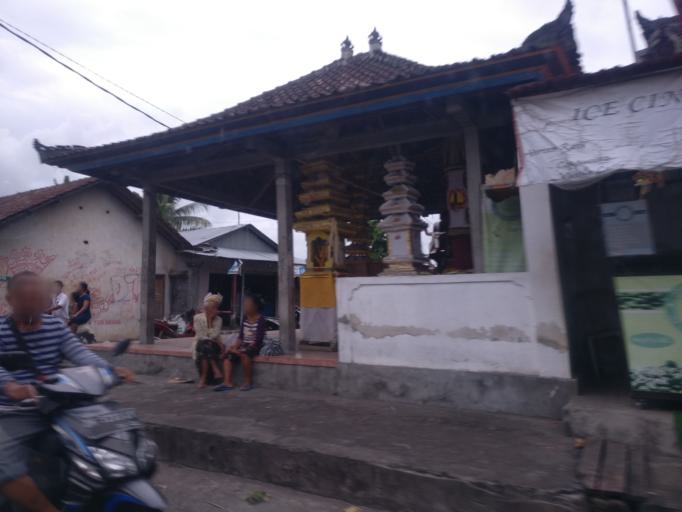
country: ID
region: Bali
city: Banjar Desa
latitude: -8.5714
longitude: 115.2969
